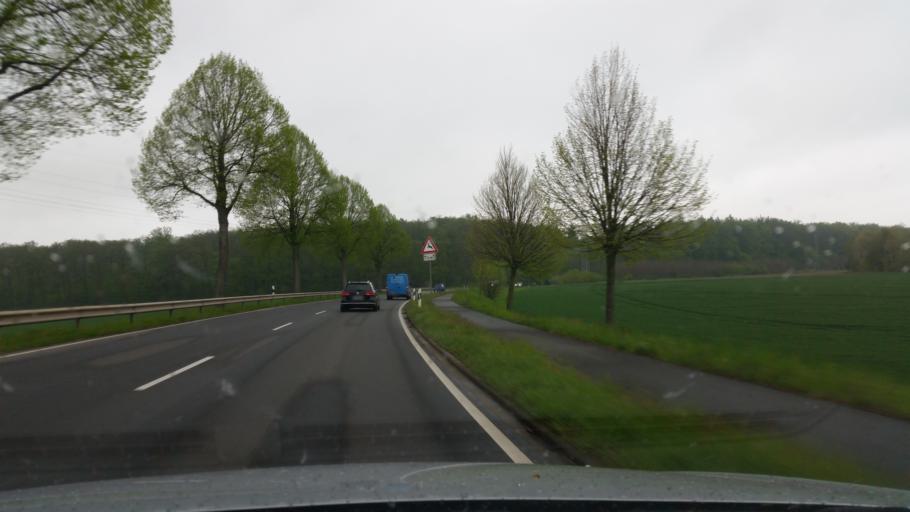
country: DE
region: Lower Saxony
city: Wolsdorf
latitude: 52.1992
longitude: 10.9680
